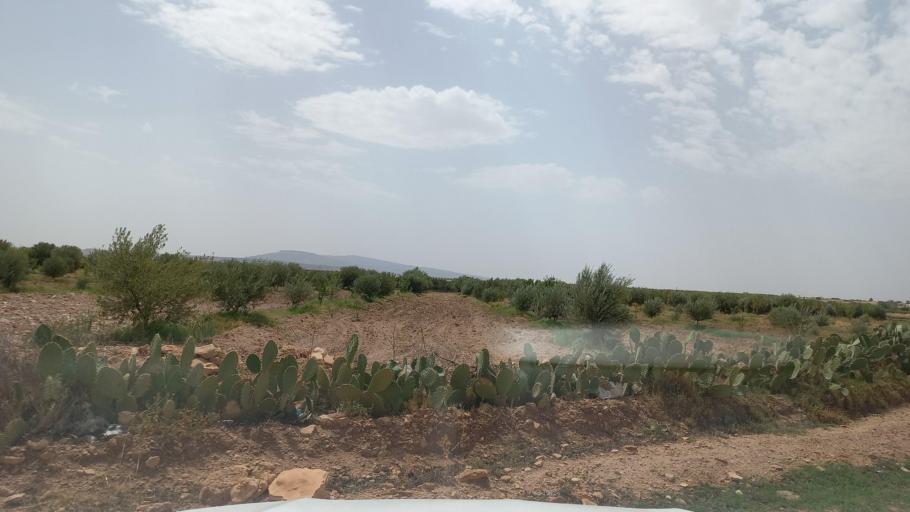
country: TN
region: Al Qasrayn
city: Kasserine
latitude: 35.2933
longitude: 9.0189
